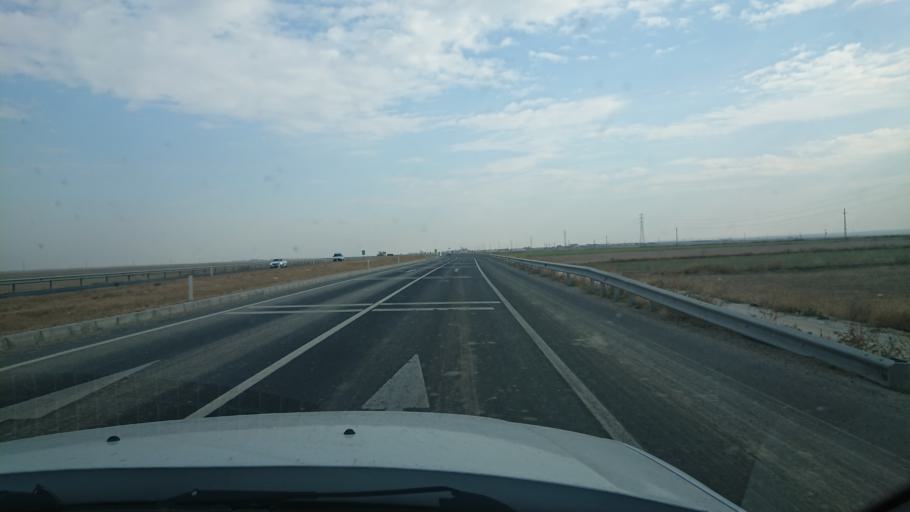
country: TR
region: Aksaray
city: Yesilova
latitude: 38.2978
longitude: 33.7870
